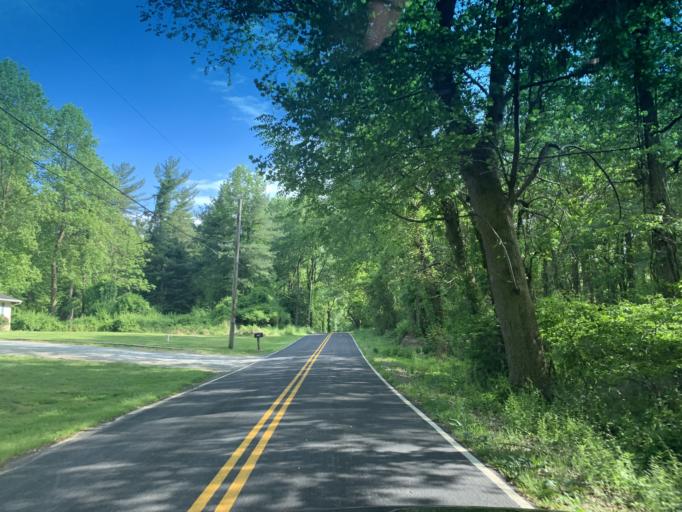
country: US
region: Maryland
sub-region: Cecil County
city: Rising Sun
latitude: 39.6928
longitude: -76.1999
